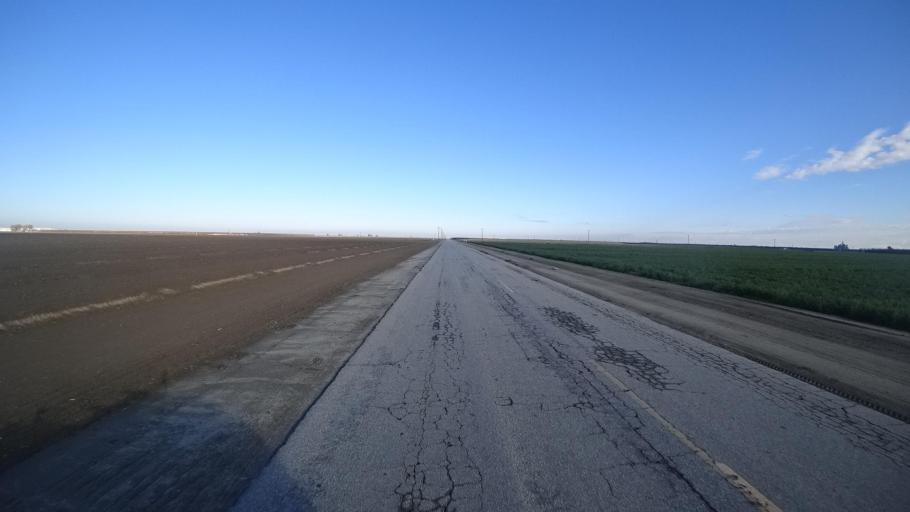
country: US
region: California
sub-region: Kern County
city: Delano
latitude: 35.7480
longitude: -119.3300
